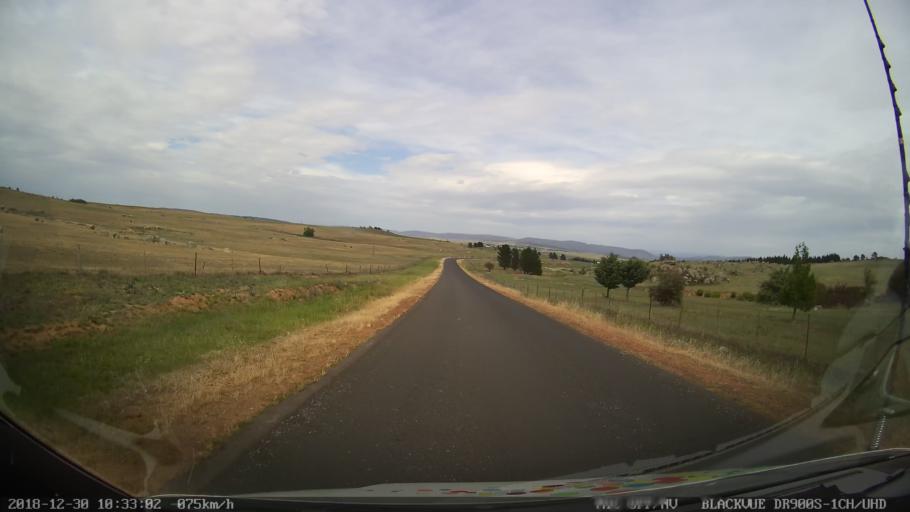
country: AU
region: New South Wales
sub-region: Snowy River
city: Berridale
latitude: -36.4986
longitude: 148.8581
